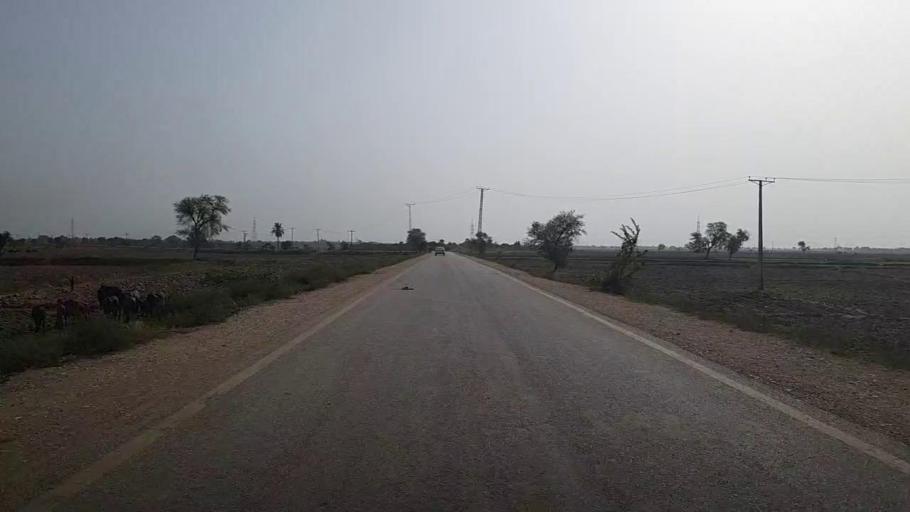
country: PK
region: Sindh
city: Khairpur Nathan Shah
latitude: 27.0979
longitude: 67.7533
